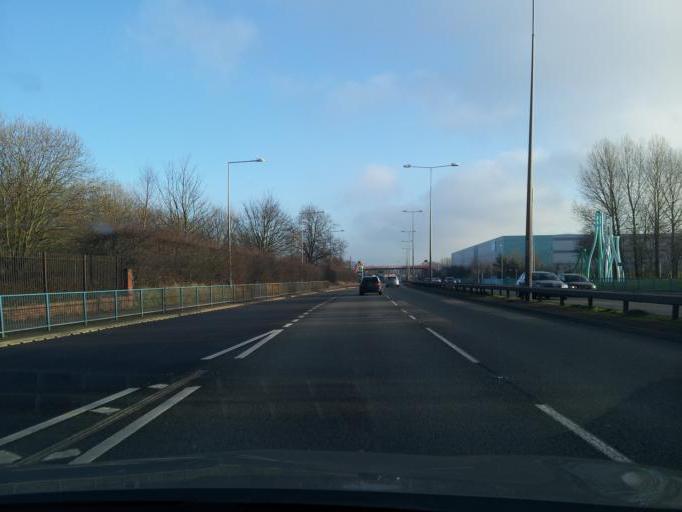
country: GB
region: England
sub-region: Staffordshire
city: Longton
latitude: 52.9759
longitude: -2.0968
